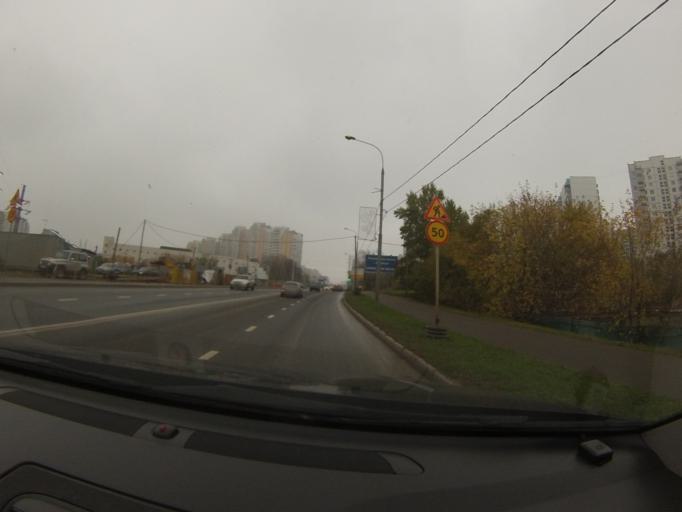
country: RU
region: Moscow
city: Nikol'skoye
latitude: 55.6887
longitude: 37.4858
